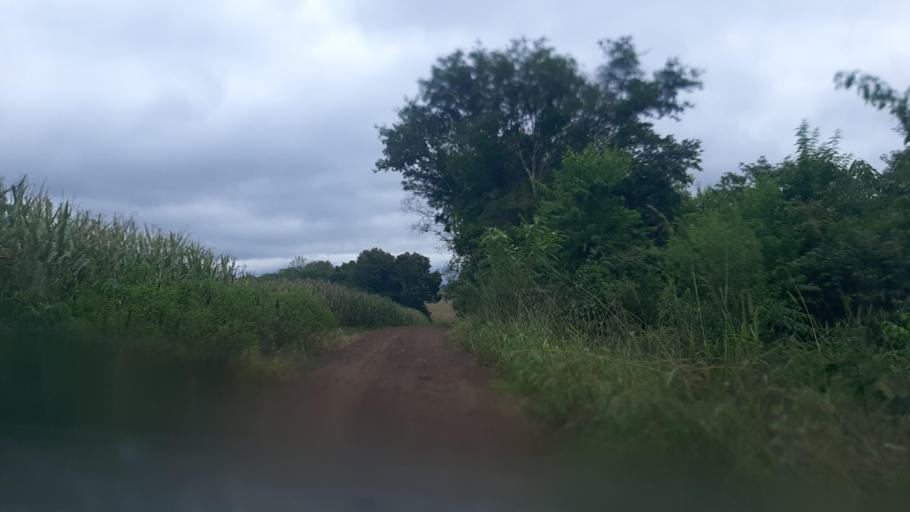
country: BR
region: Parana
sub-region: Ampere
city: Ampere
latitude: -26.0497
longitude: -53.5294
